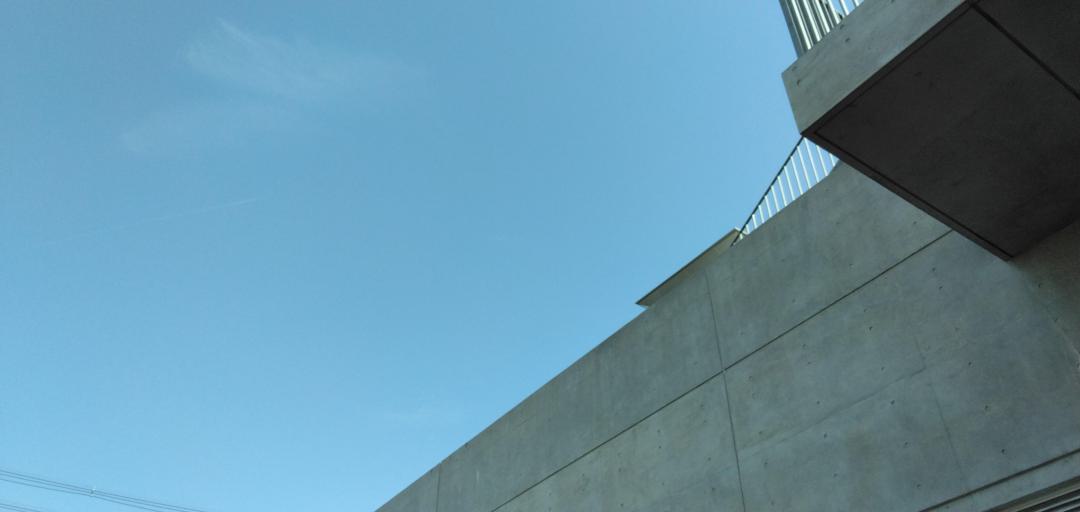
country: JP
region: Osaka
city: Sakai
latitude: 34.5641
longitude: 135.4694
